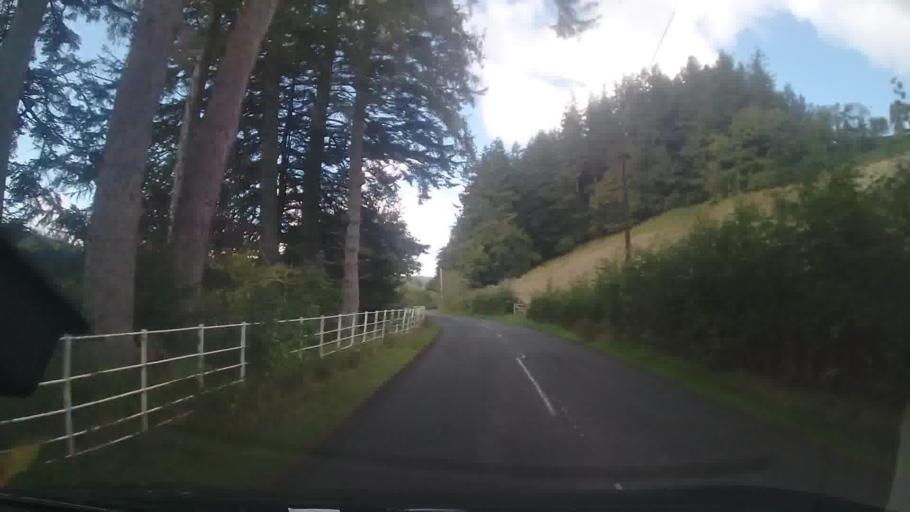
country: GB
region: Wales
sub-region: Sir Powys
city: Llangynog
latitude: 52.7691
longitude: -3.4603
